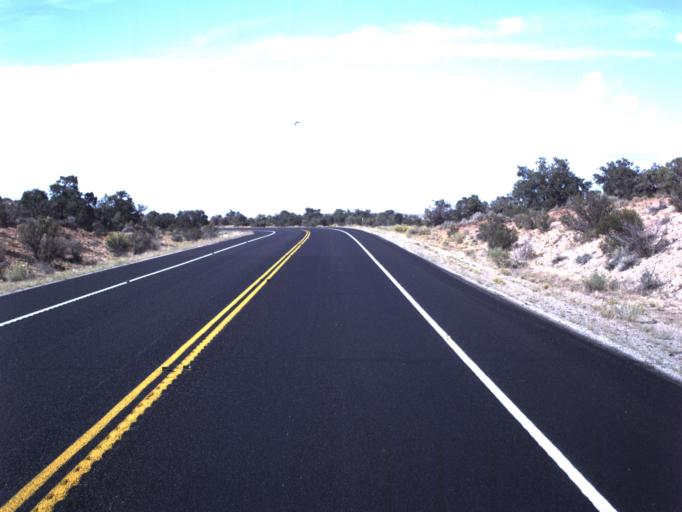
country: US
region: Utah
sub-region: Grand County
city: Moab
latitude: 38.5574
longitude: -109.7926
